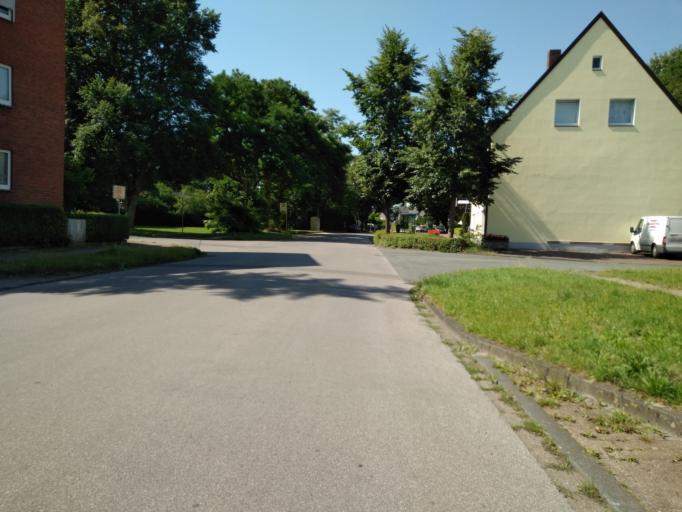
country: DE
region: North Rhine-Westphalia
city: Dorsten
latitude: 51.6777
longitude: 6.9444
